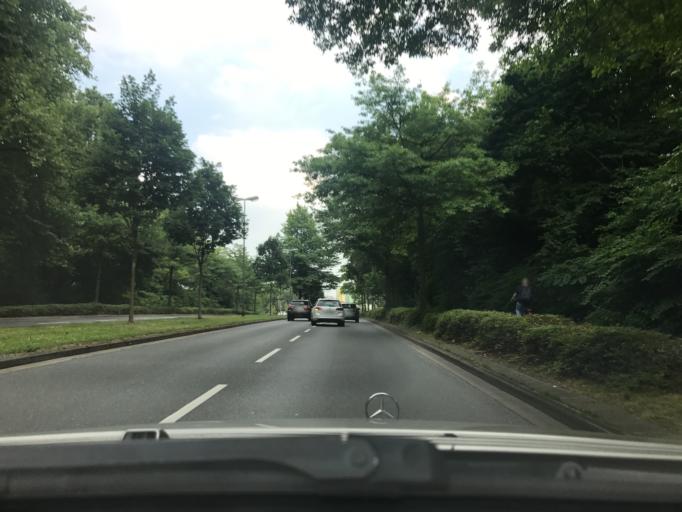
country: DE
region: North Rhine-Westphalia
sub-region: Regierungsbezirk Dusseldorf
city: Essen
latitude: 51.4690
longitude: 6.9972
